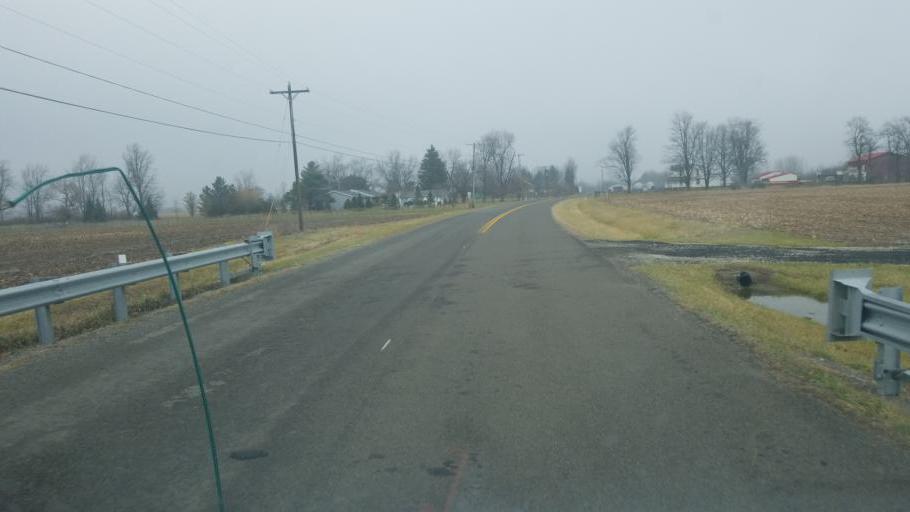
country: US
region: Ohio
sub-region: Champaign County
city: North Lewisburg
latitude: 40.3398
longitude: -83.5646
